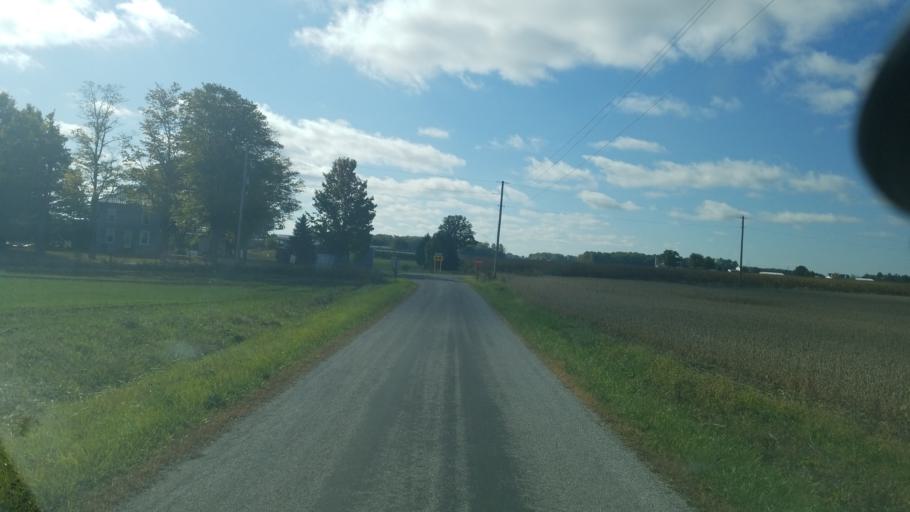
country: US
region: Ohio
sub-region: Morrow County
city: Mount Gilead
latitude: 40.6511
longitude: -82.9007
